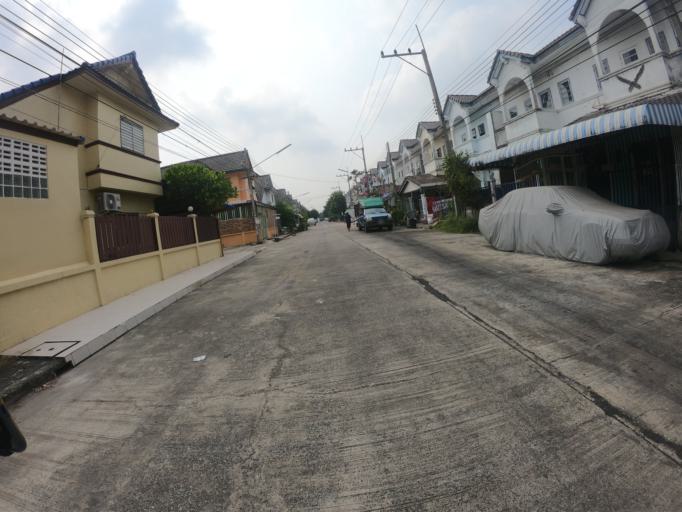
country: TH
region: Pathum Thani
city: Nong Suea
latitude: 14.0785
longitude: 100.8584
